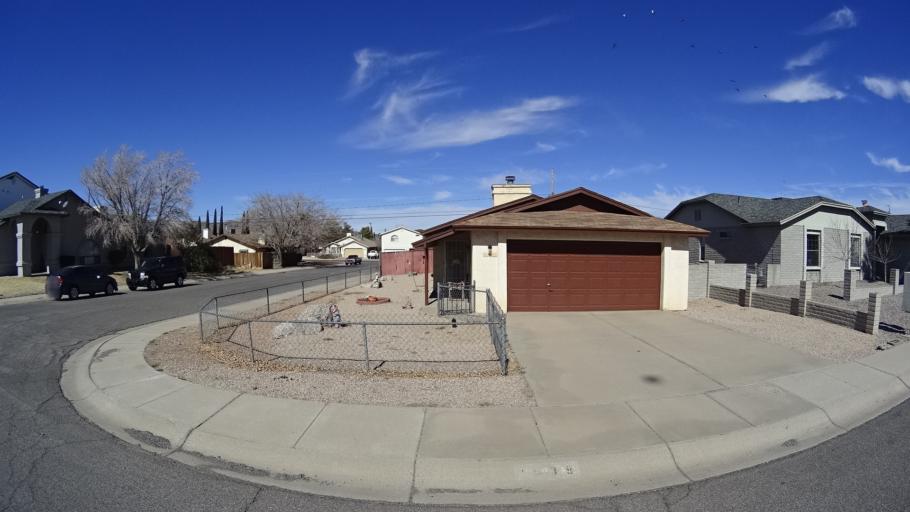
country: US
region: Arizona
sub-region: Mohave County
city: Kingman
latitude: 35.2060
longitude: -114.0362
